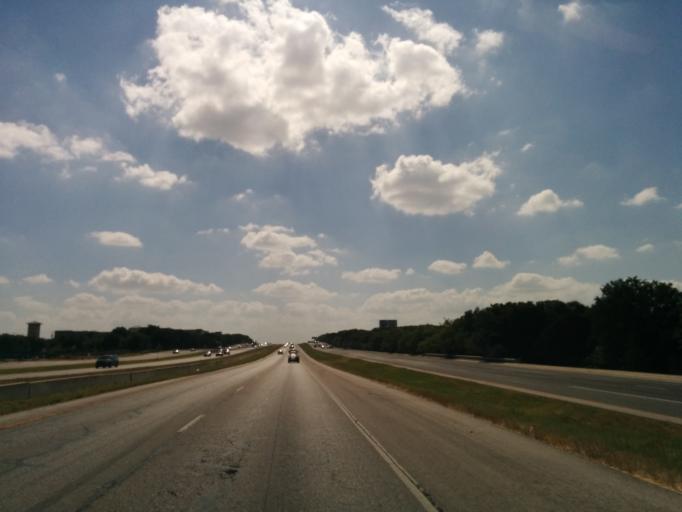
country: US
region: Texas
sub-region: Bexar County
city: Shavano Park
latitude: 29.6020
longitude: -98.5461
